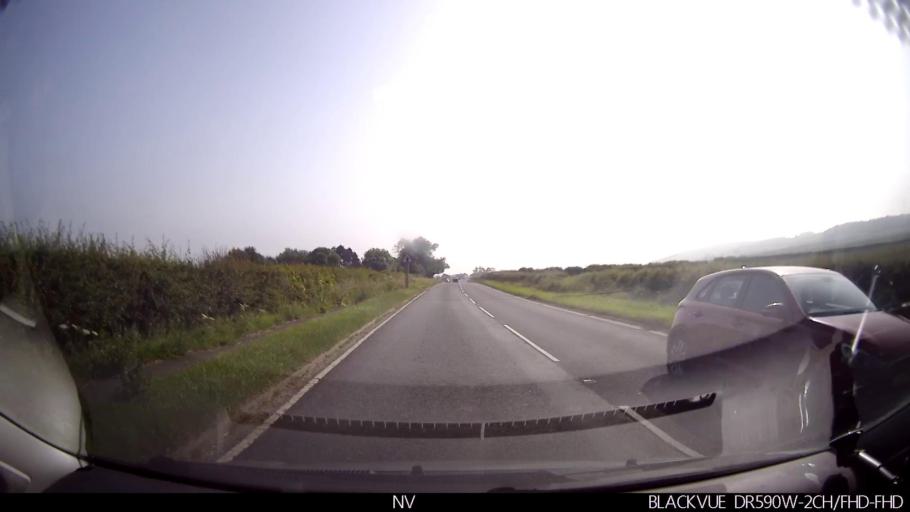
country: GB
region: England
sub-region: North Yorkshire
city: East Ayton
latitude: 54.1911
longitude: -0.4752
